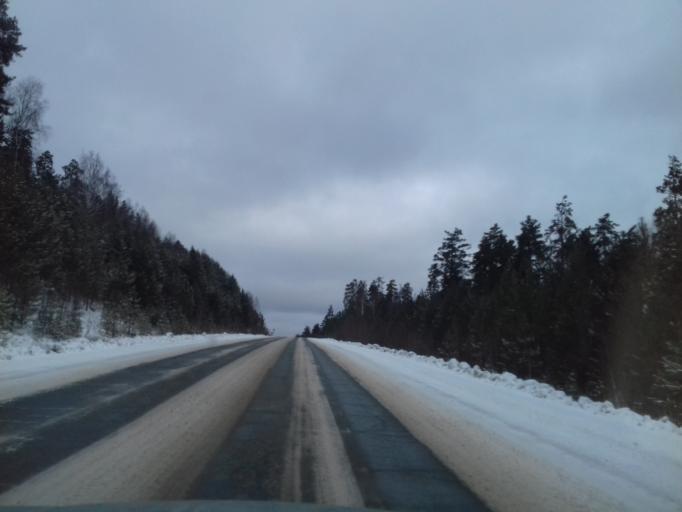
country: RU
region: Bashkortostan
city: Verkhniy Avzyan
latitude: 53.5605
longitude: 57.7131
